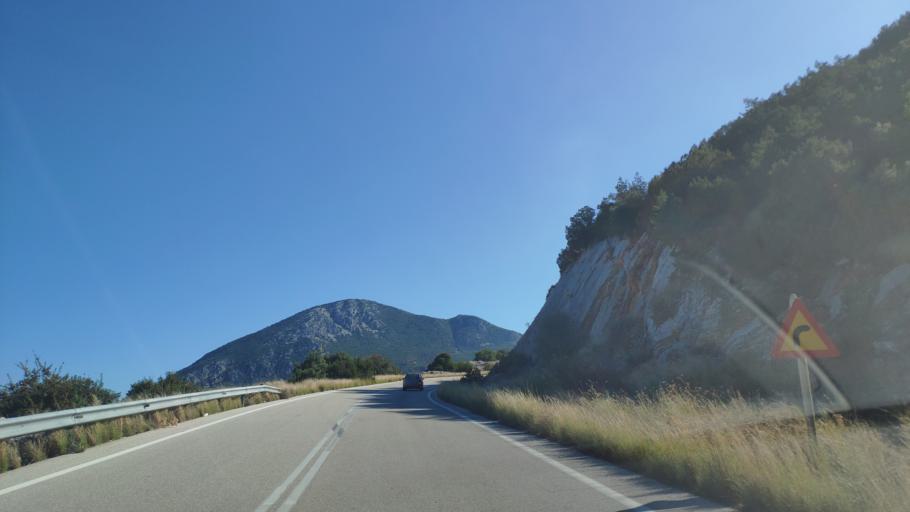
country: GR
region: Peloponnese
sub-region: Nomos Argolidos
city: Palaia Epidavros
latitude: 37.6190
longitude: 23.1482
